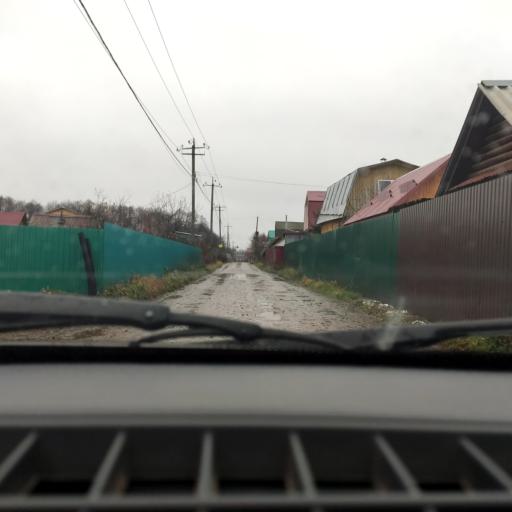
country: RU
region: Bashkortostan
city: Avdon
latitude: 54.6248
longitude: 55.7316
